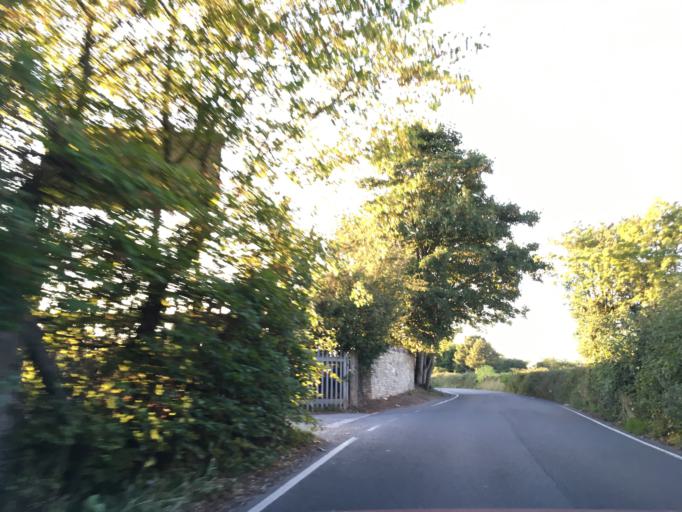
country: GB
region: England
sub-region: Bath and North East Somerset
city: Whitchurch
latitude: 51.4247
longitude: -2.5353
